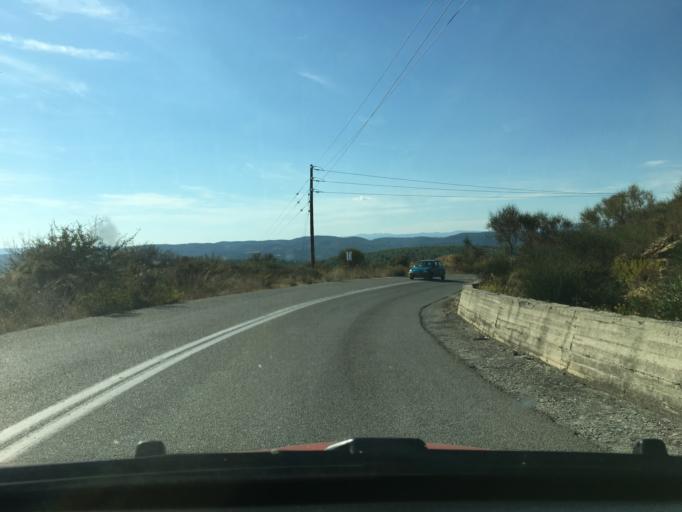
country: GR
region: Central Macedonia
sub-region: Nomos Chalkidikis
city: Ierissos
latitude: 40.3834
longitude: 23.8247
